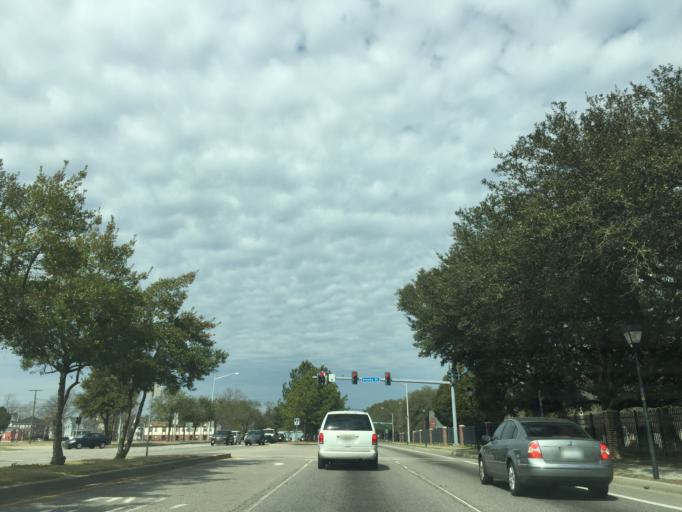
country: US
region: Virginia
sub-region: City of Norfolk
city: Norfolk
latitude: 36.8743
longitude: -76.2812
